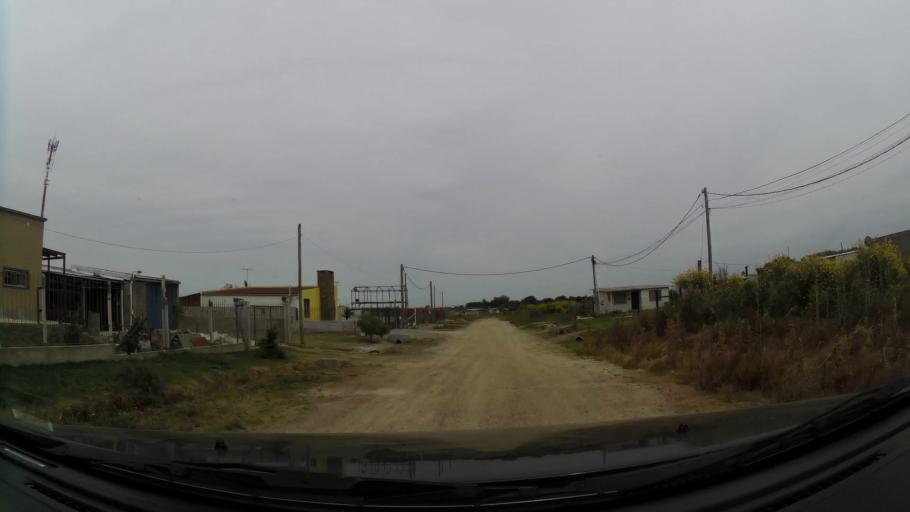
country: UY
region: Canelones
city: La Paz
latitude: -34.7454
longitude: -56.2279
